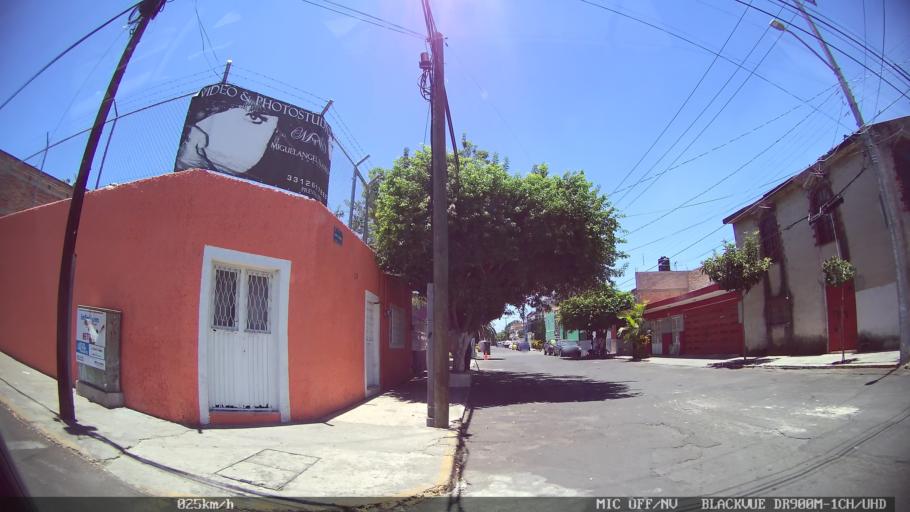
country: MX
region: Jalisco
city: Tlaquepaque
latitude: 20.6758
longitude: -103.2894
